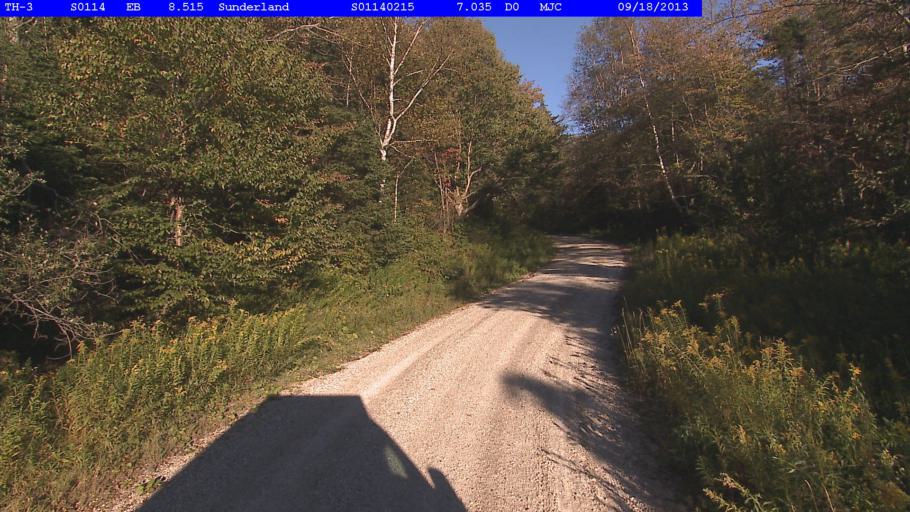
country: US
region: Vermont
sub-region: Bennington County
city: Arlington
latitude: 43.0522
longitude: -73.0485
